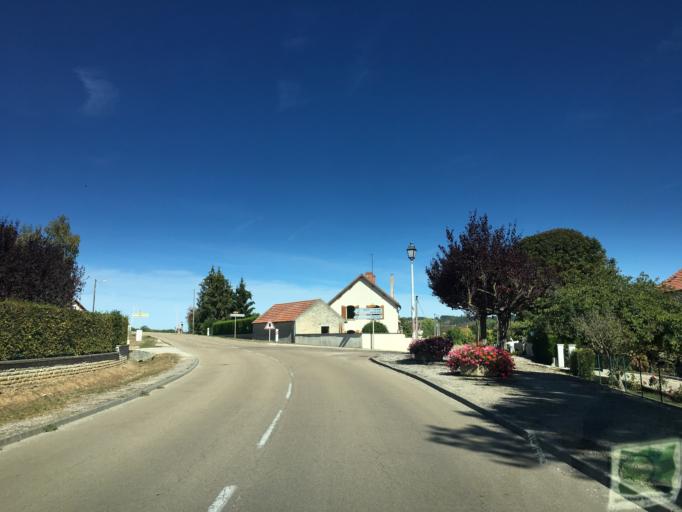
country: FR
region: Bourgogne
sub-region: Departement de l'Yonne
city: Vermenton
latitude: 47.6076
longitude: 3.6788
